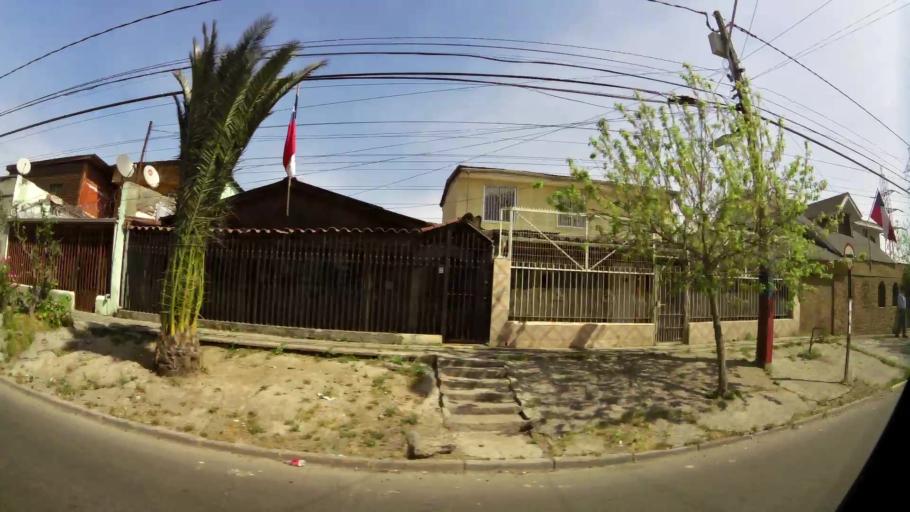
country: CL
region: Santiago Metropolitan
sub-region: Provincia de Santiago
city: Lo Prado
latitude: -33.4309
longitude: -70.7305
